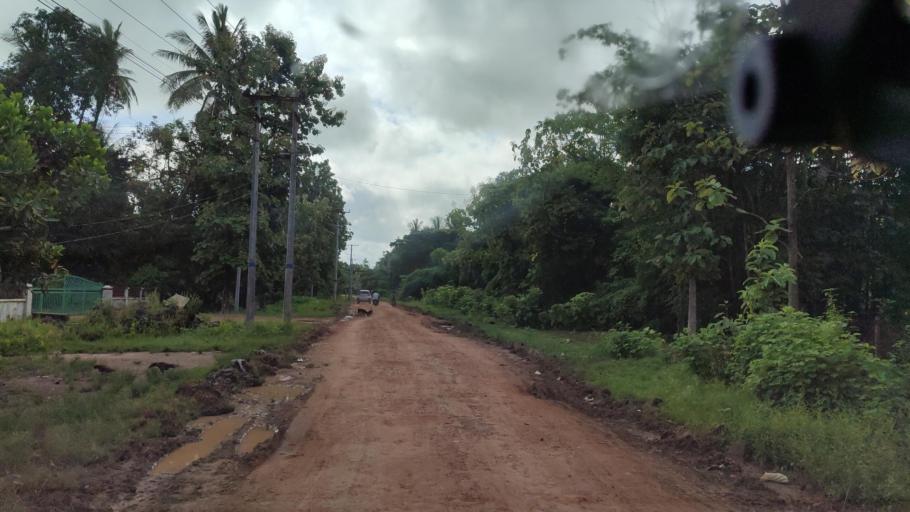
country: MM
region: Bago
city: Letpandan
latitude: 17.8955
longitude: 95.7135
